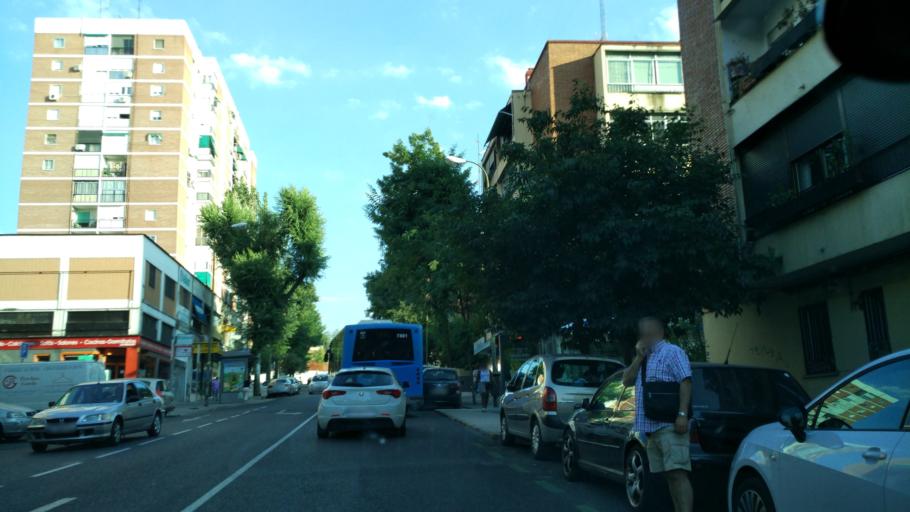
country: ES
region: Madrid
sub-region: Provincia de Madrid
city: Tetuan de las Victorias
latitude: 40.4766
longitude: -3.7117
